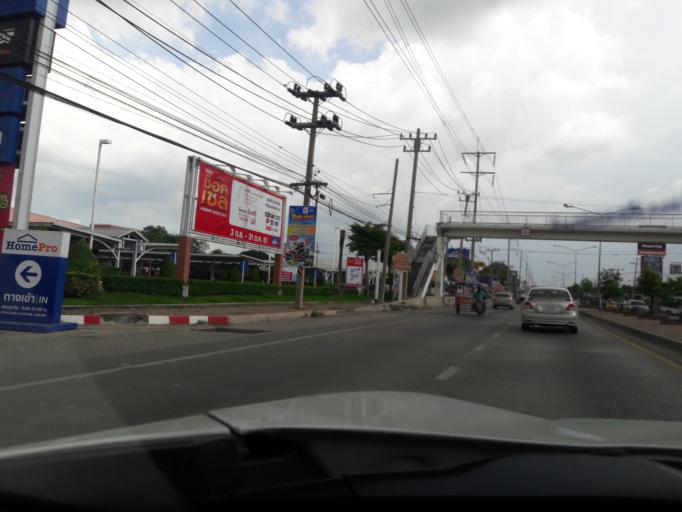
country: TH
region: Lop Buri
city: Lop Buri
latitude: 14.7841
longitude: 100.6833
